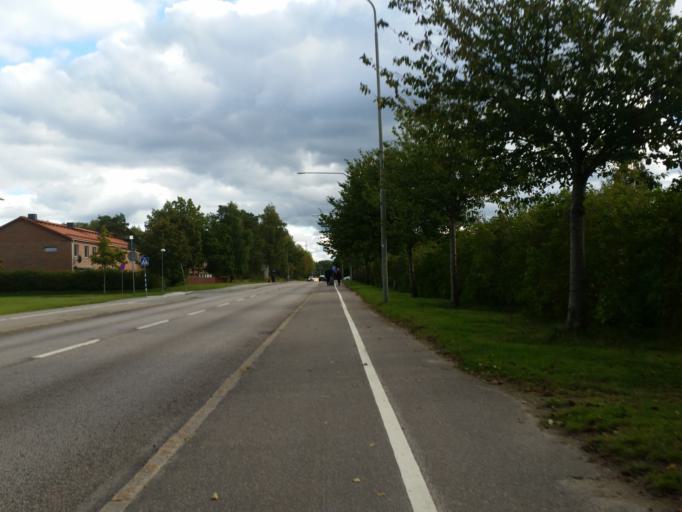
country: SE
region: Stockholm
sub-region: Nacka Kommun
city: Nacka
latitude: 59.2676
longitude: 18.1173
